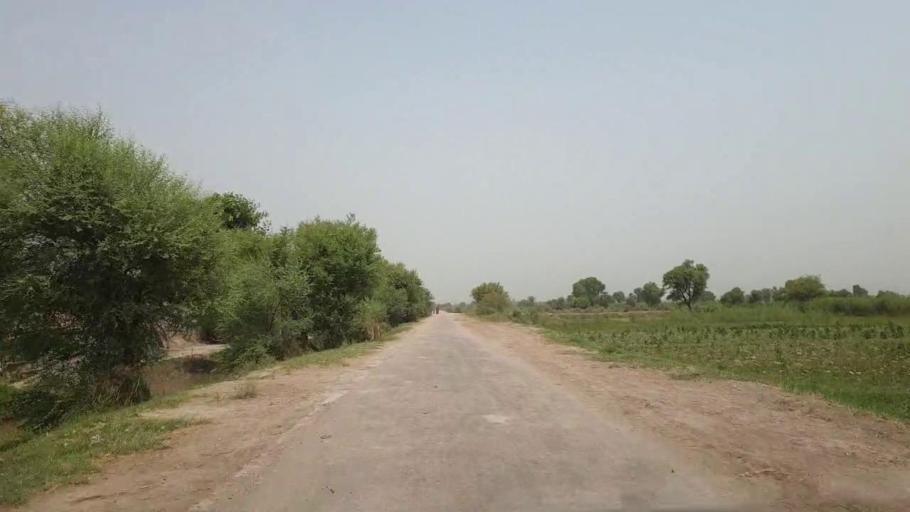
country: PK
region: Sindh
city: Gambat
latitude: 27.4451
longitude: 68.4452
